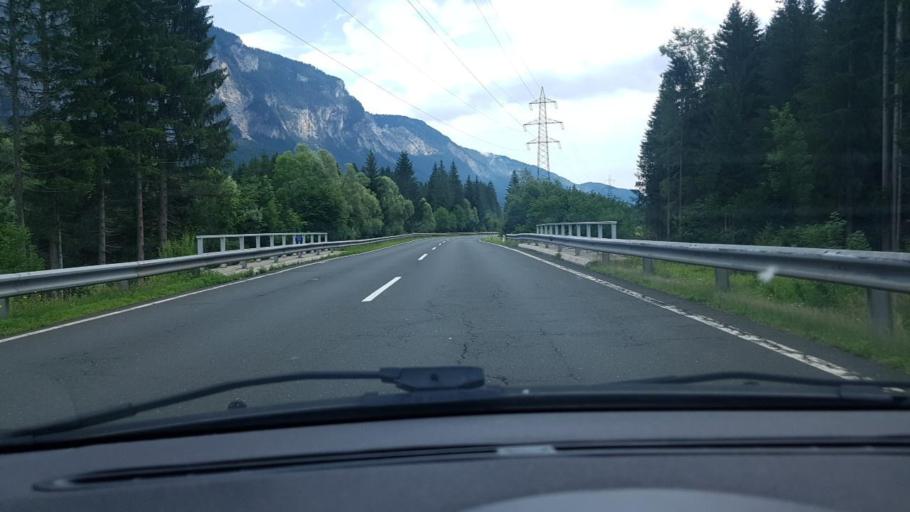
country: AT
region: Carinthia
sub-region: Politischer Bezirk Villach Land
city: Hohenthurn
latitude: 46.5680
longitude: 13.6727
